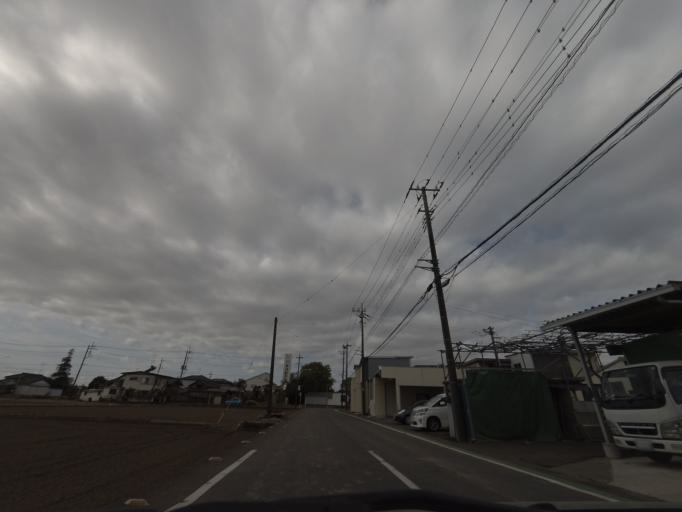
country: JP
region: Saitama
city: Kamifukuoka
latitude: 35.8906
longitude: 139.5468
